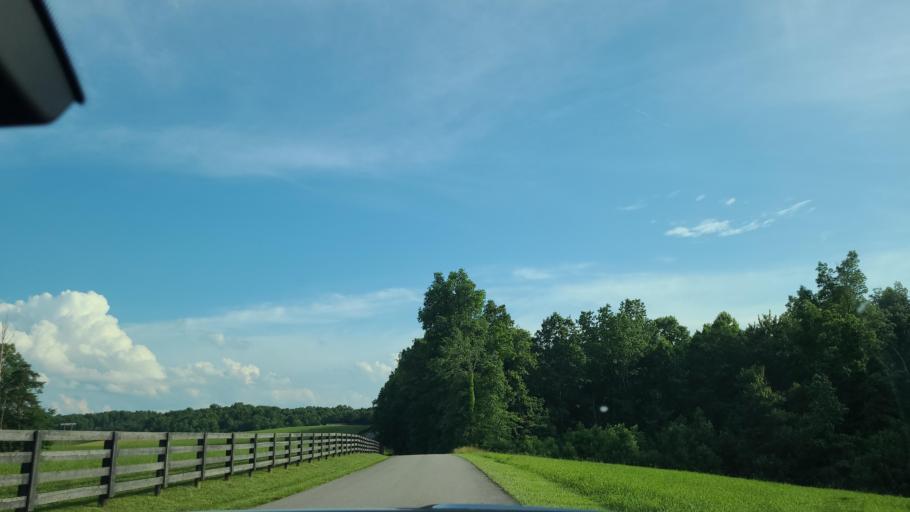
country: US
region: Kentucky
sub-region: Whitley County
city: Corbin
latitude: 36.8898
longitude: -84.2342
